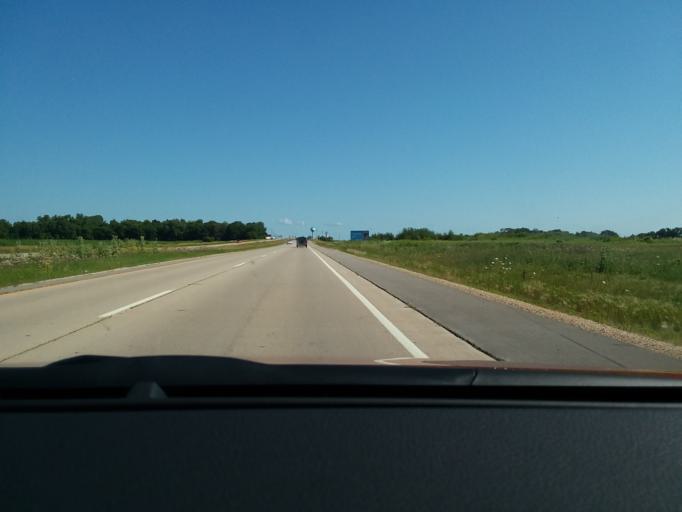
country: US
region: Wisconsin
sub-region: Dane County
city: Windsor
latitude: 43.1575
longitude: -89.3246
